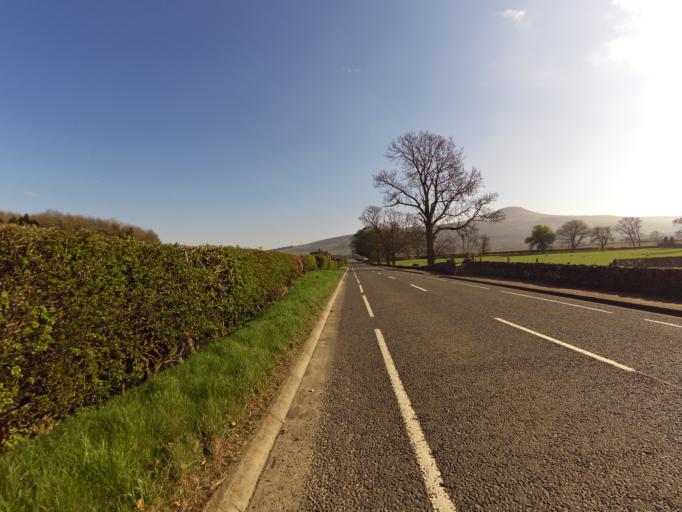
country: GB
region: Scotland
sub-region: Fife
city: Falkland
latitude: 56.2663
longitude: -3.2094
